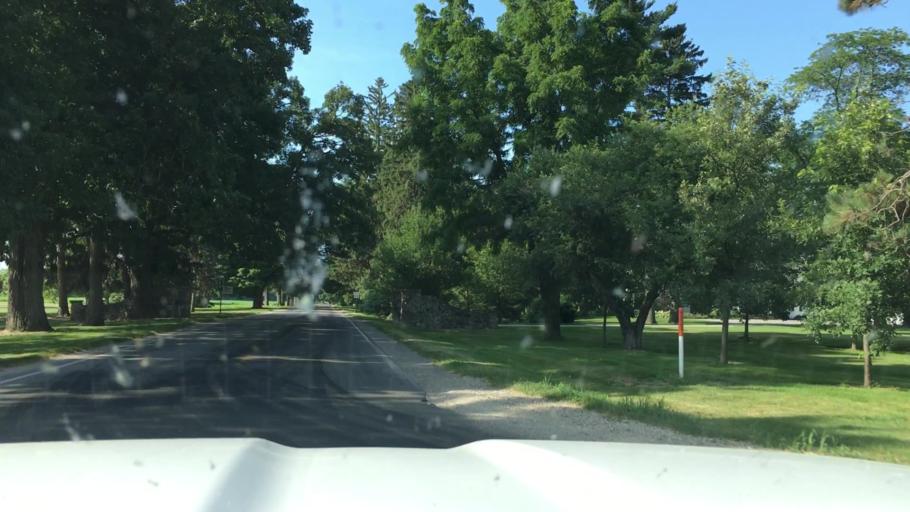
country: US
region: Michigan
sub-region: Kalamazoo County
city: South Gull Lake
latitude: 42.4279
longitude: -85.4546
